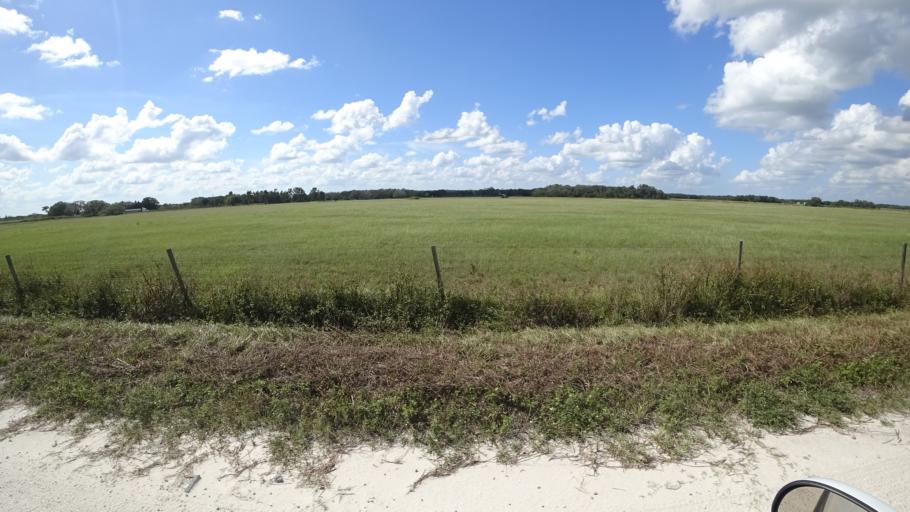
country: US
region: Florida
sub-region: DeSoto County
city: Arcadia
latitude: 27.3164
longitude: -82.1051
